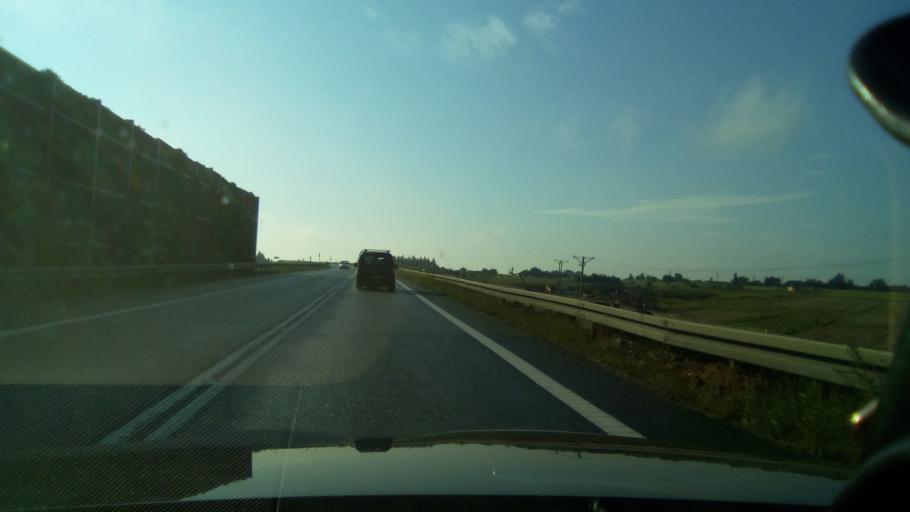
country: PL
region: Silesian Voivodeship
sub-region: Powiat bedzinski
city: Mierzecice
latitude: 50.4465
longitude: 19.1381
